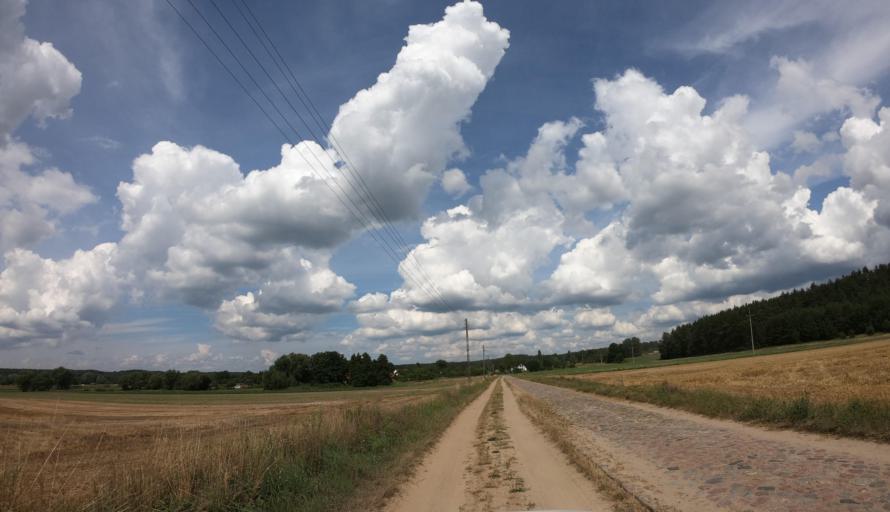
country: PL
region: West Pomeranian Voivodeship
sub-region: Powiat stargardzki
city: Kobylanka
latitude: 53.3193
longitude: 14.8261
